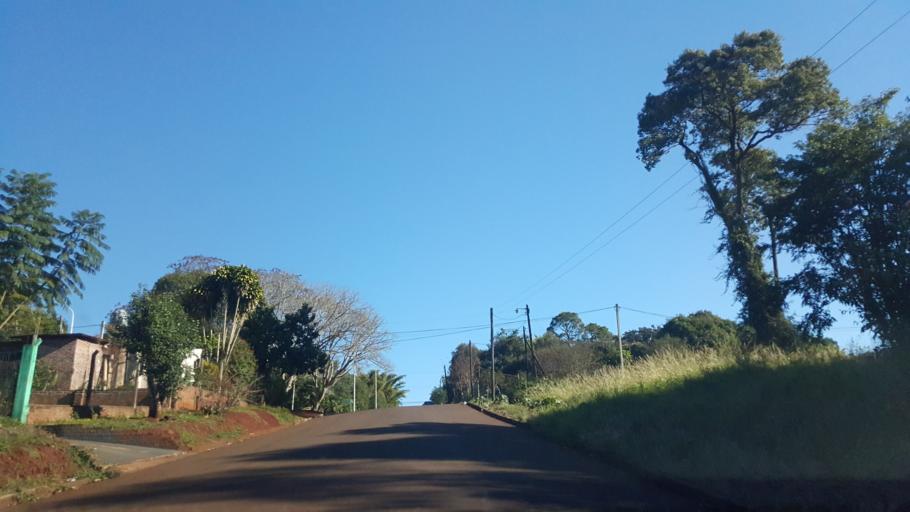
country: AR
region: Misiones
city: Gobernador Roca
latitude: -27.1890
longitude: -55.4688
